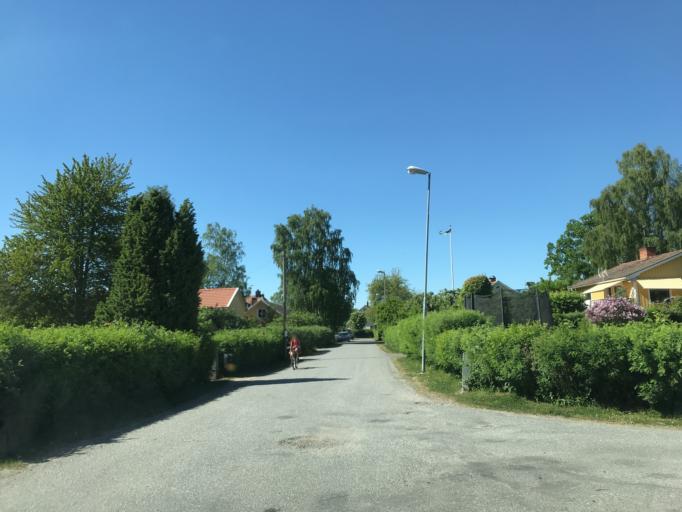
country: SE
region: Stockholm
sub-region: Sollentuna Kommun
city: Sollentuna
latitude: 59.4219
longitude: 17.9616
